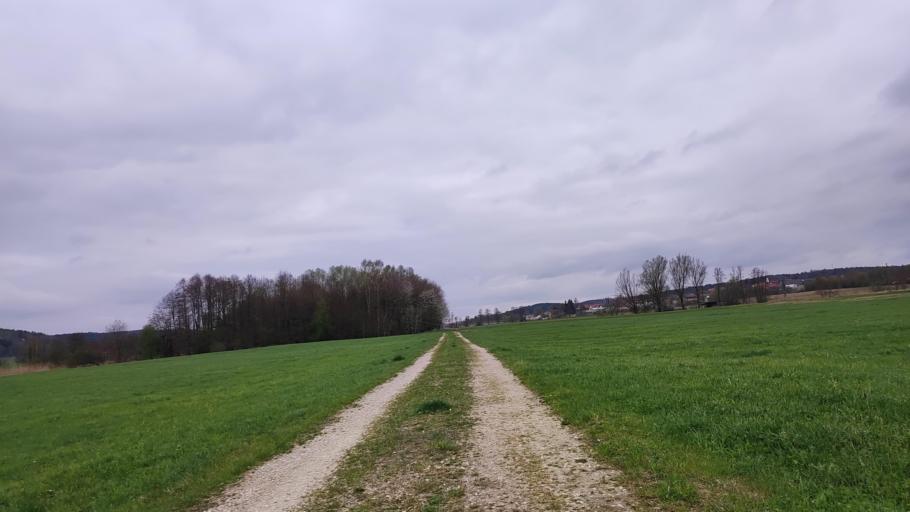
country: DE
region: Bavaria
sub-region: Swabia
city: Altenmunster
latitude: 48.4543
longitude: 10.5925
